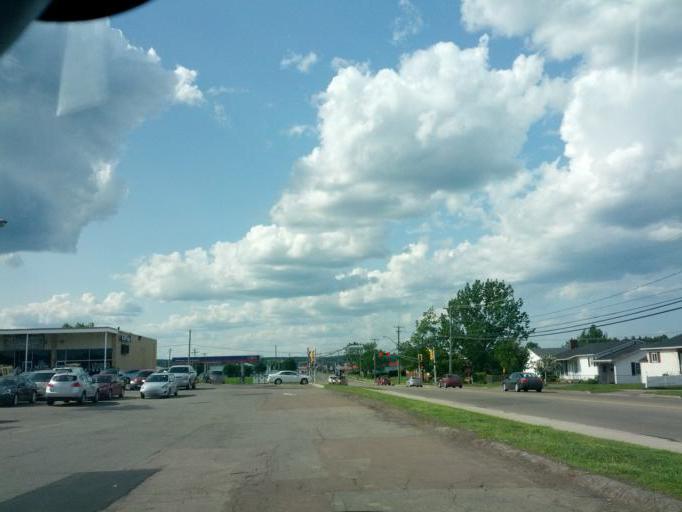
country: CA
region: New Brunswick
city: Moncton
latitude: 46.1086
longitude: -64.8233
